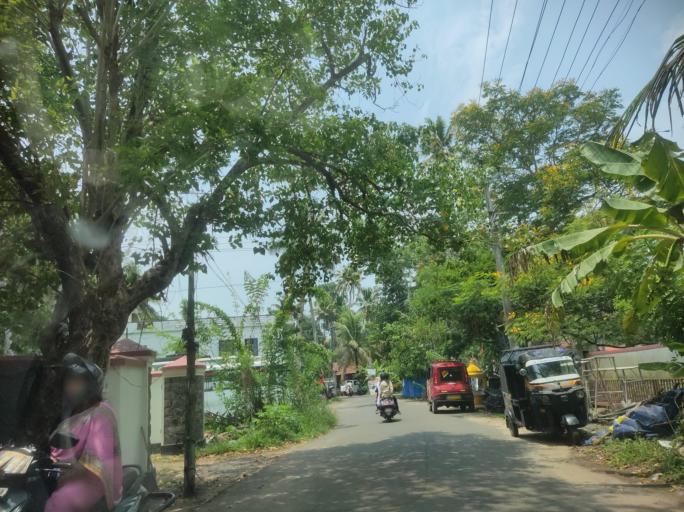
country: IN
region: Kerala
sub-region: Alappuzha
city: Vayalar
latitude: 9.7377
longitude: 76.3260
